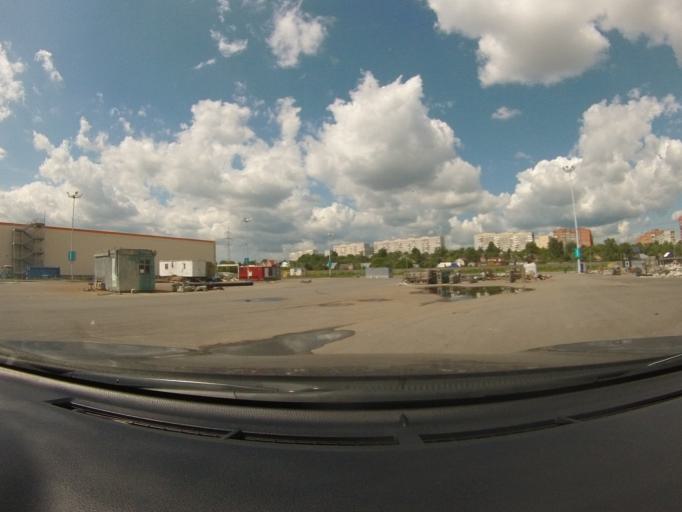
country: RU
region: Tula
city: Tula
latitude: 54.1929
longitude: 37.6417
